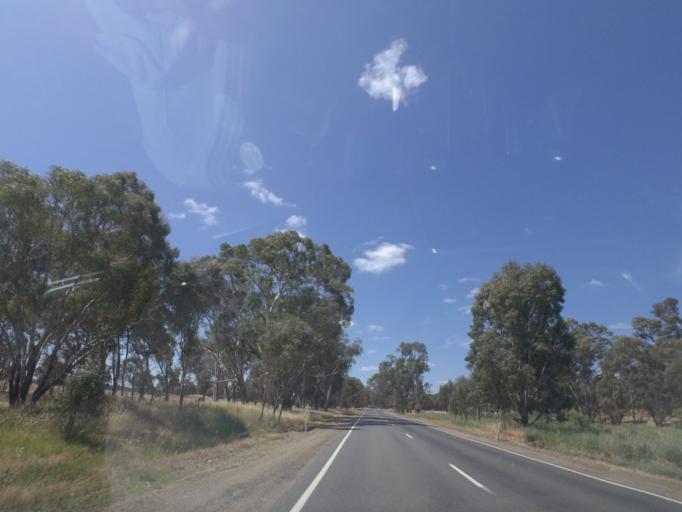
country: AU
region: Victoria
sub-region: Wangaratta
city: Wangaratta
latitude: -36.4088
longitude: 146.2706
